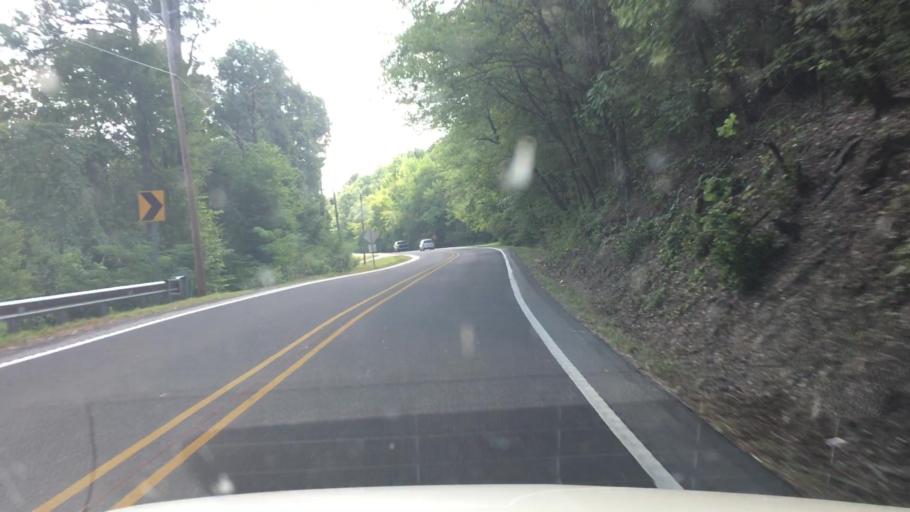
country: US
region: Arkansas
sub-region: Garland County
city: Piney
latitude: 34.5098
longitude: -93.1685
